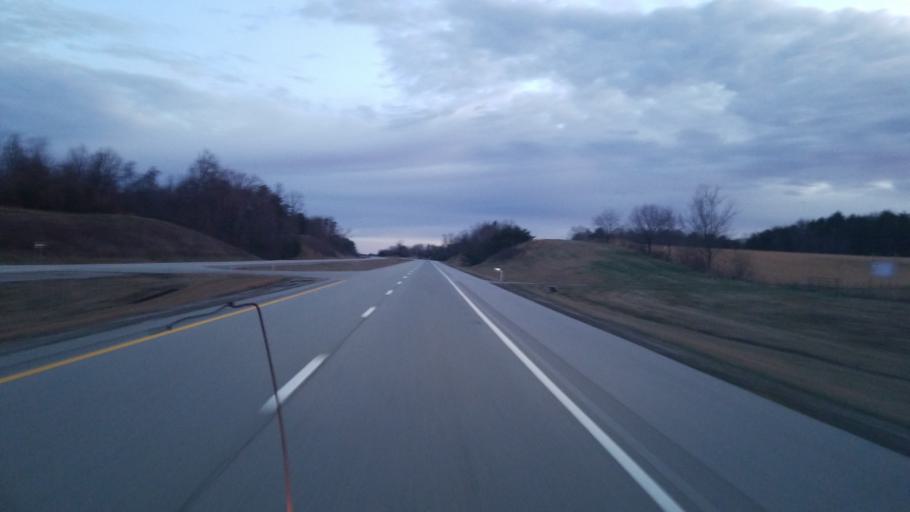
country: US
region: Tennessee
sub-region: Van Buren County
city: Spencer
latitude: 35.7001
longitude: -85.4792
